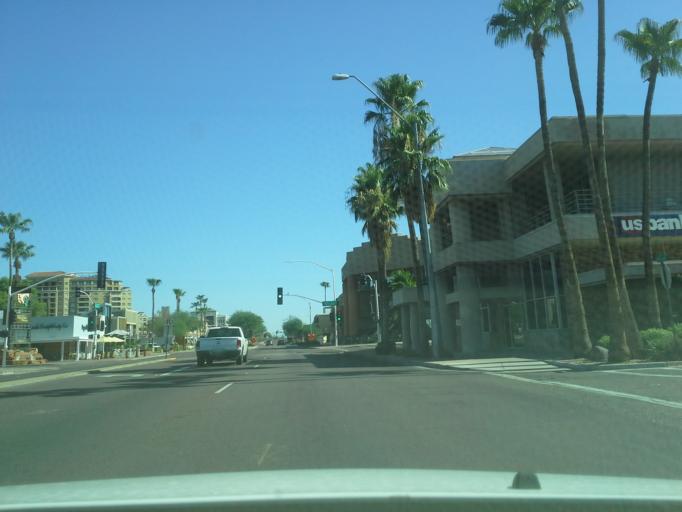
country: US
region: Arizona
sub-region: Maricopa County
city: Scottsdale
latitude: 33.4977
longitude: -111.9260
